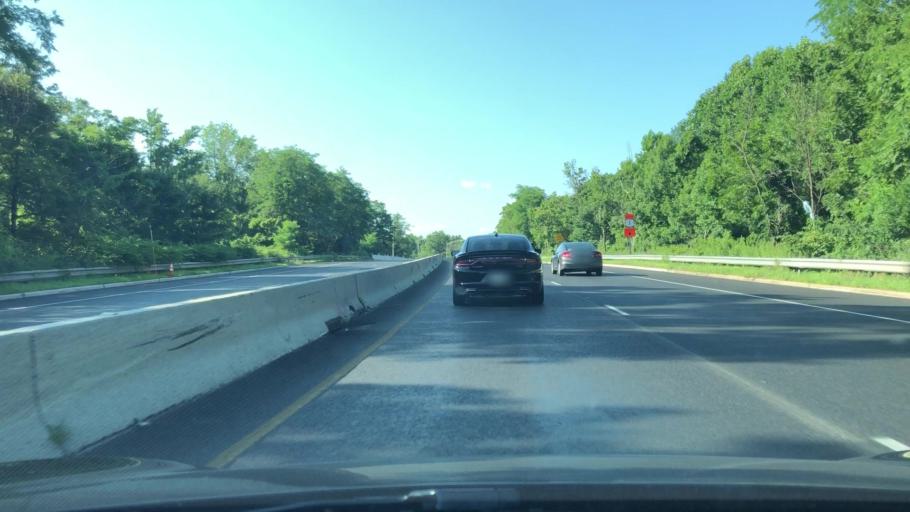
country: US
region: New Jersey
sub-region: Mercer County
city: Lawrenceville
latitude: 40.2645
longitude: -74.7152
